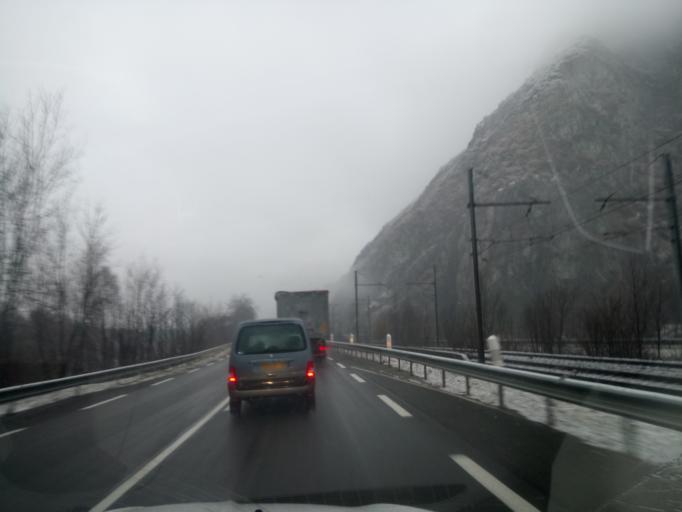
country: FR
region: Rhone-Alpes
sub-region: Departement de la Savoie
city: La Chambre
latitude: 45.3691
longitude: 6.2878
